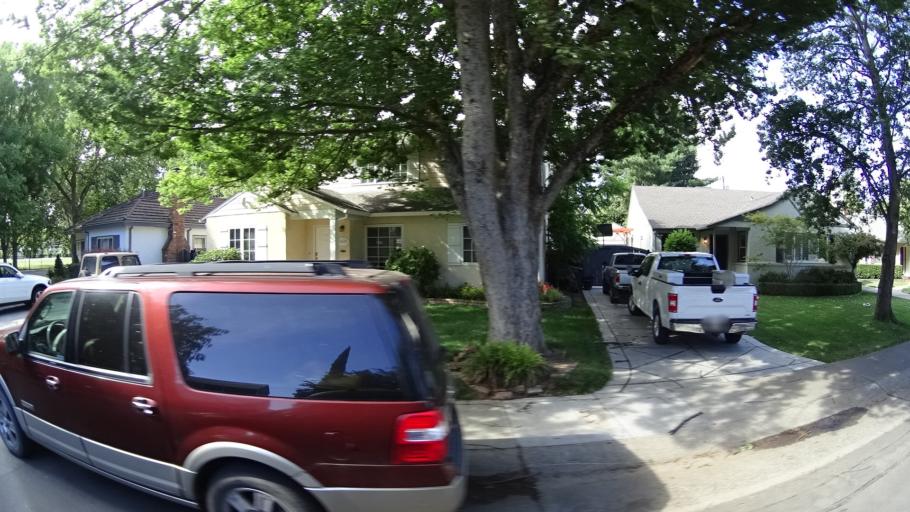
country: US
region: California
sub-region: Sacramento County
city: Sacramento
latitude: 38.5521
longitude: -121.4988
